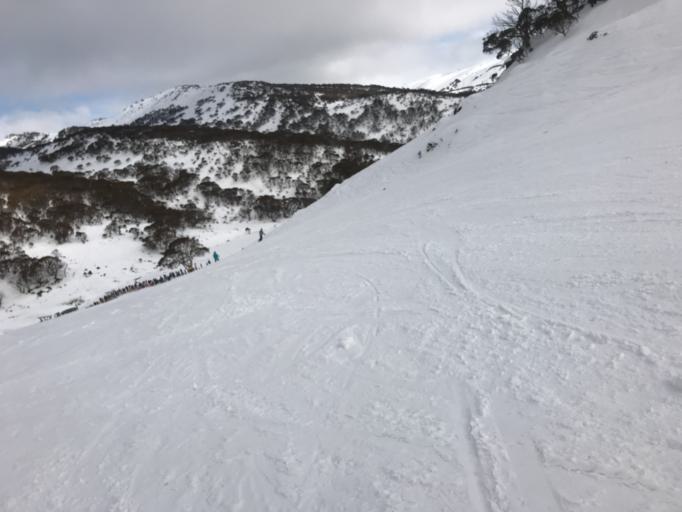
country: AU
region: New South Wales
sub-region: Snowy River
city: Jindabyne
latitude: -36.3835
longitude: 148.3792
